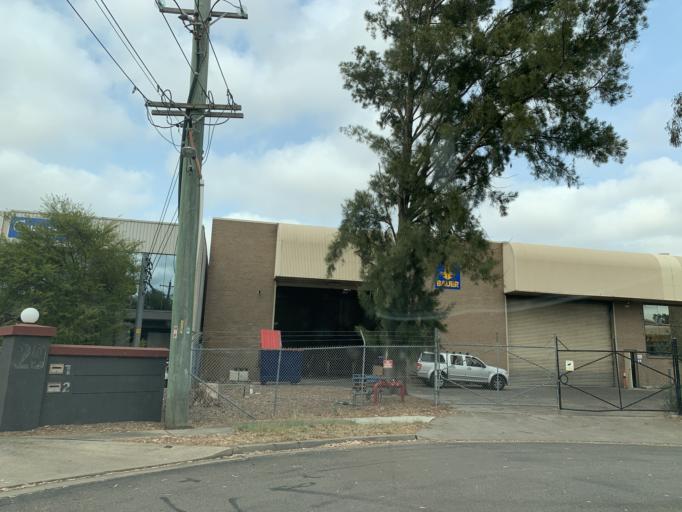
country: AU
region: New South Wales
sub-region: Parramatta
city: Constitution Hill
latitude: -33.7723
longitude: 150.9554
